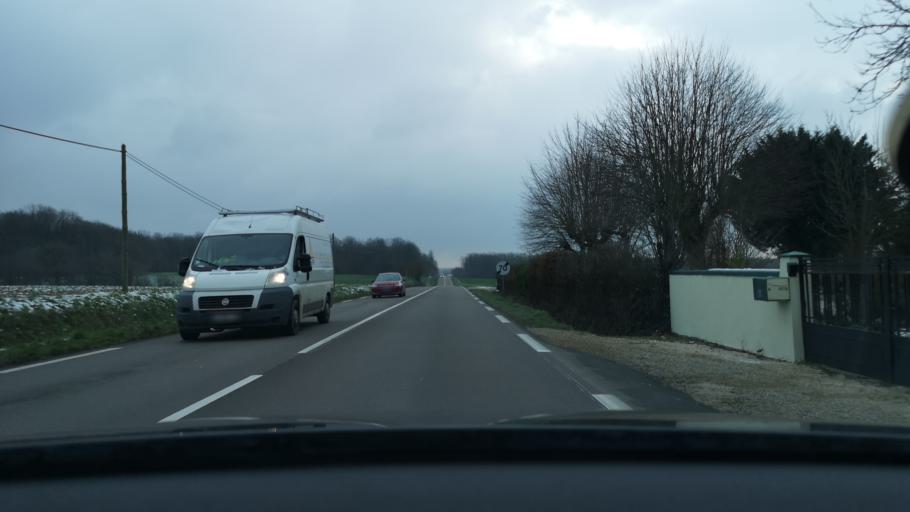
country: FR
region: Bourgogne
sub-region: Departement de Saone-et-Loire
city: Ouroux-sur-Saone
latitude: 46.7691
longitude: 4.9793
